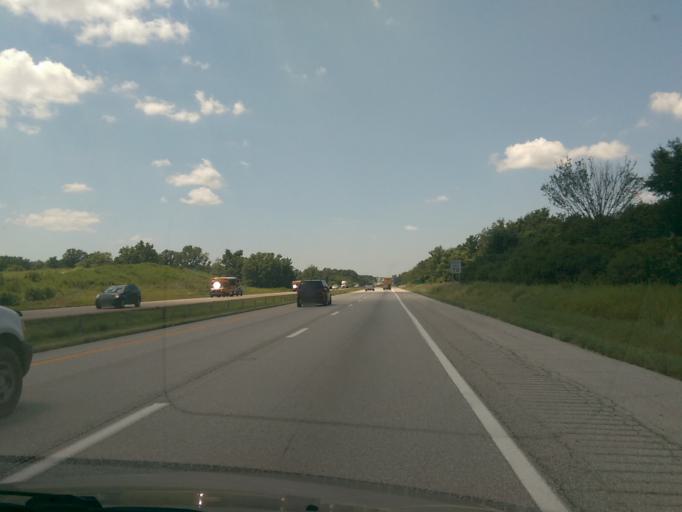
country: US
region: Missouri
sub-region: Cooper County
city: Boonville
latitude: 38.9376
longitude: -92.6994
